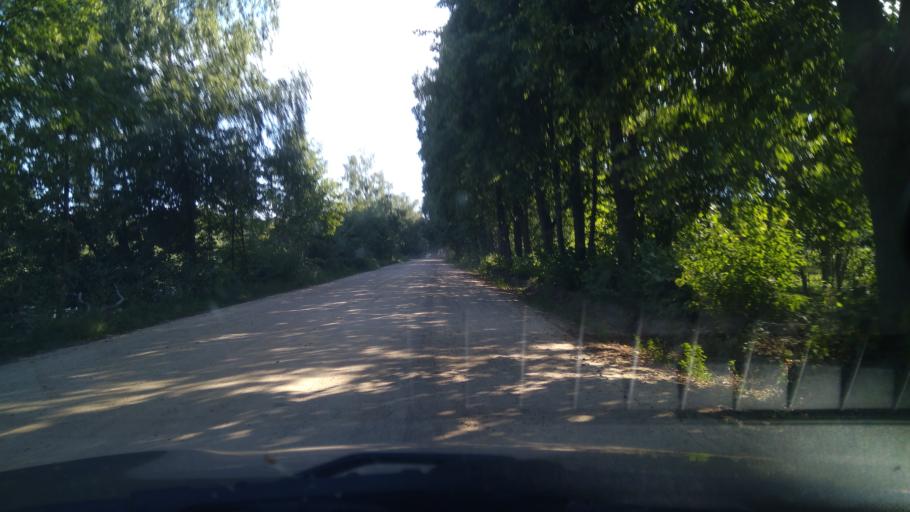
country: BY
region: Brest
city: Byelaazyorsk
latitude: 52.4482
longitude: 25.1802
